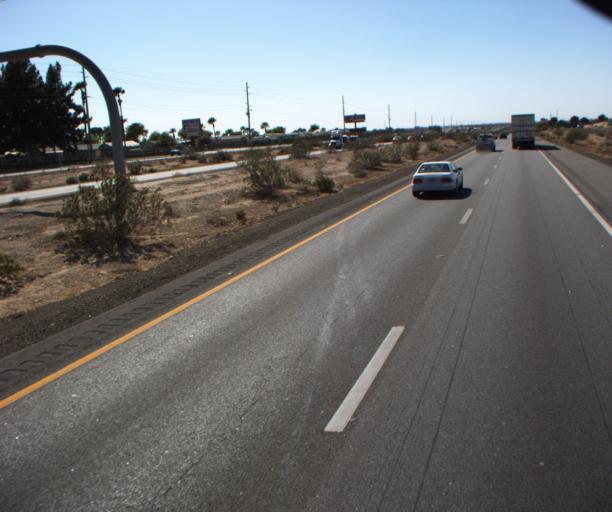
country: US
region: Arizona
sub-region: Yuma County
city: Fortuna Foothills
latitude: 32.6708
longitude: -114.4619
